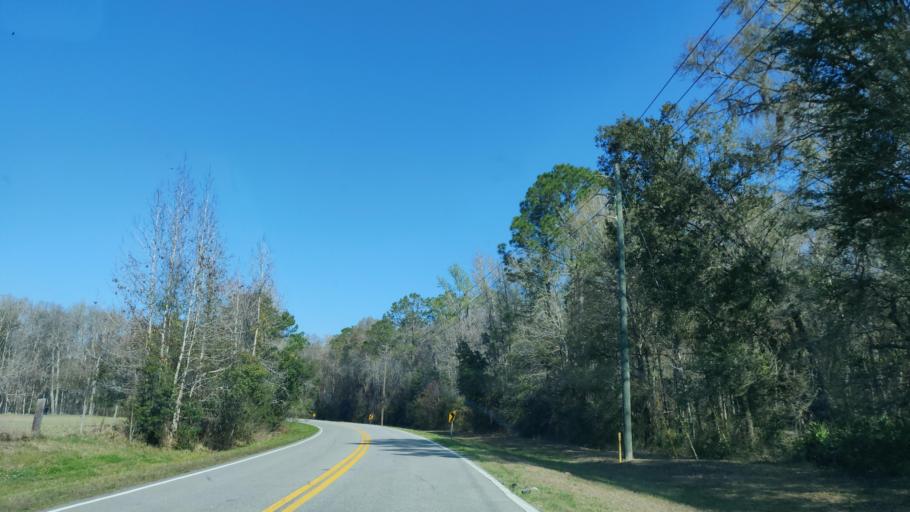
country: US
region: Florida
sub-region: Duval County
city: Baldwin
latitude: 30.2422
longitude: -81.9412
